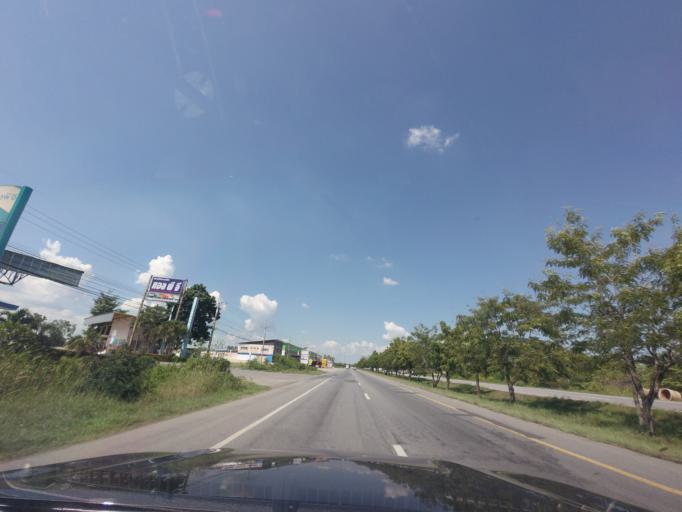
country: TH
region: Nakhon Ratchasima
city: Non Sung
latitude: 15.1739
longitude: 102.3360
